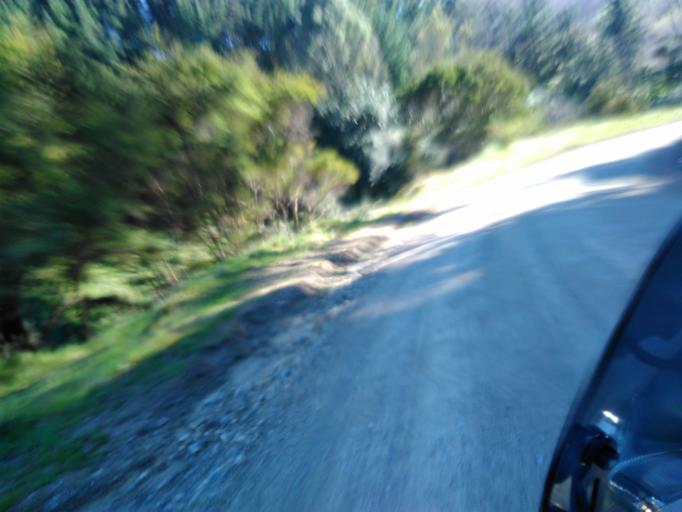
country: NZ
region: Gisborne
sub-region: Gisborne District
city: Gisborne
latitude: -38.3910
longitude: 177.6615
